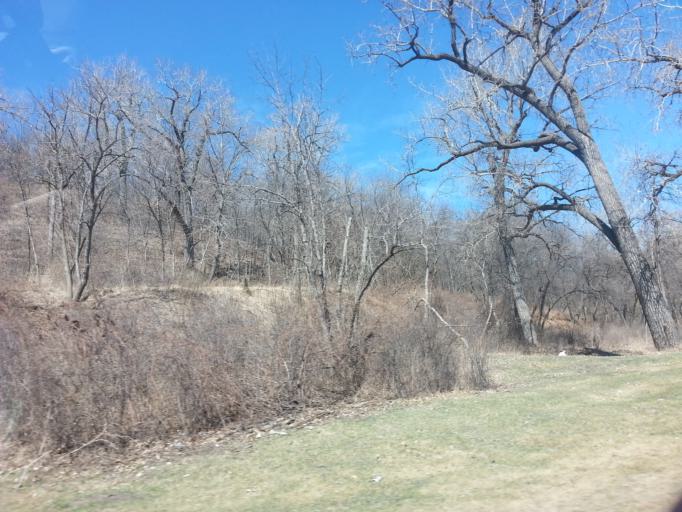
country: US
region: Minnesota
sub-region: Ramsey County
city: Saint Paul
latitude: 44.9452
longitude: -93.0486
